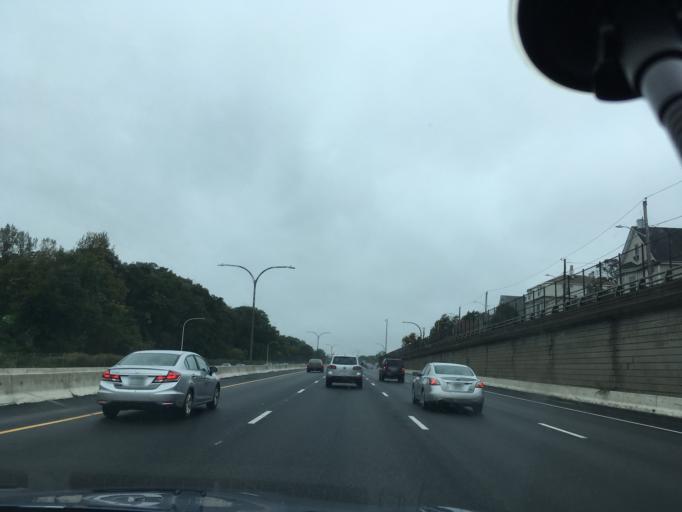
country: US
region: Rhode Island
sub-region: Providence County
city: Cranston
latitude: 41.7936
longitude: -71.4110
